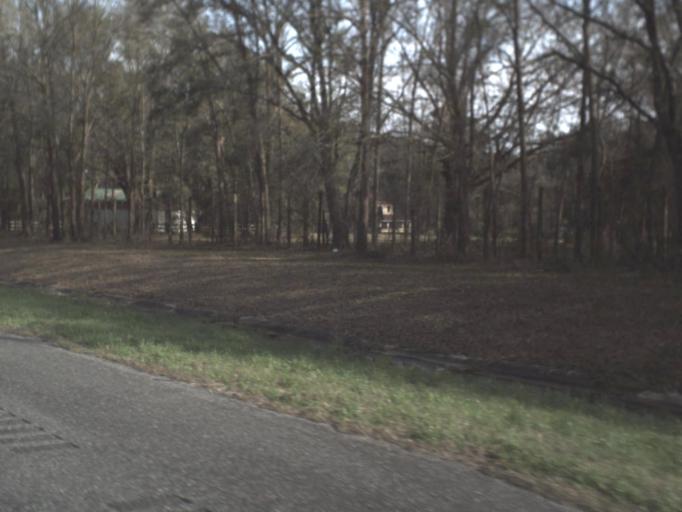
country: US
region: Florida
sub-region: Leon County
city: Tallahassee
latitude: 30.4779
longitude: -84.0726
